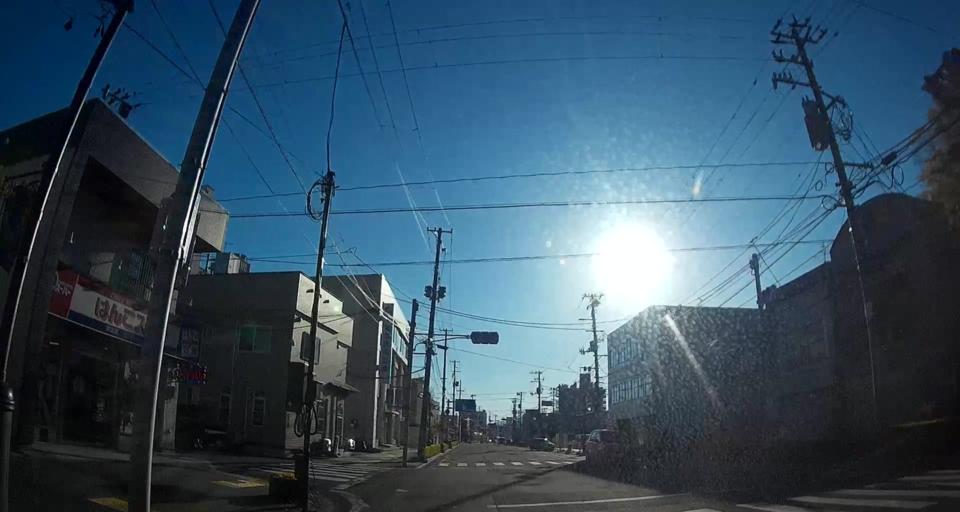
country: JP
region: Iwate
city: Miyako
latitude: 39.6424
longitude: 141.9558
